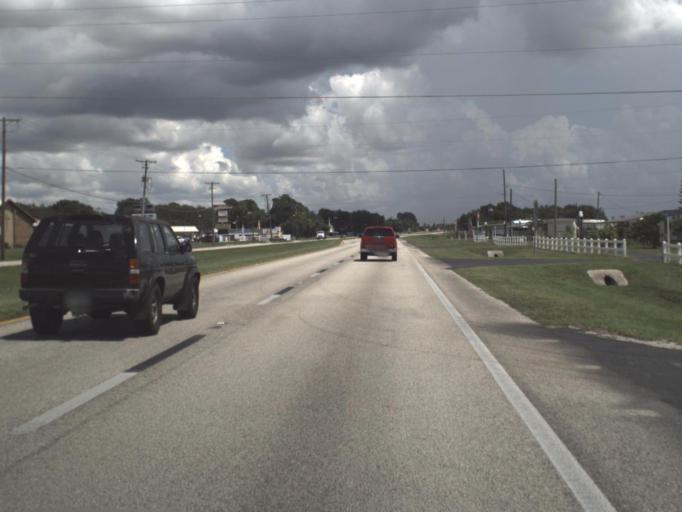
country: US
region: Florida
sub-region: Polk County
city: Auburndale
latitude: 28.0646
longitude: -81.7665
